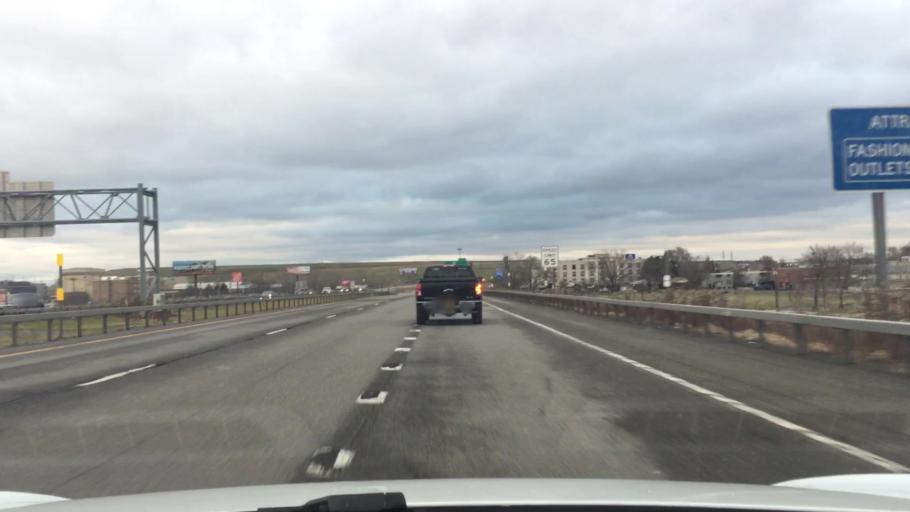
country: US
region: New York
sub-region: Niagara County
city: Niagara Falls
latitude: 43.0842
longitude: -78.9906
